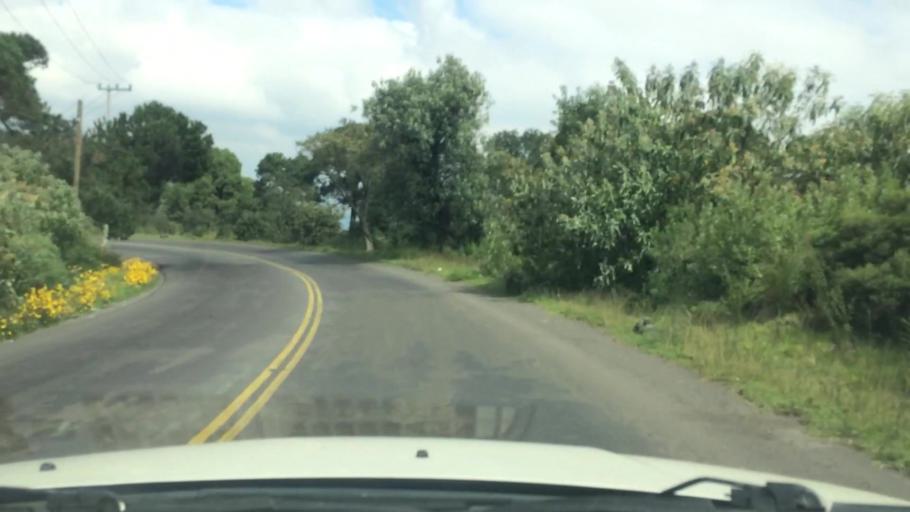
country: MX
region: Mexico City
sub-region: Tlalpan
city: Lomas de Tepemecatl
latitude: 19.2601
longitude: -99.2371
